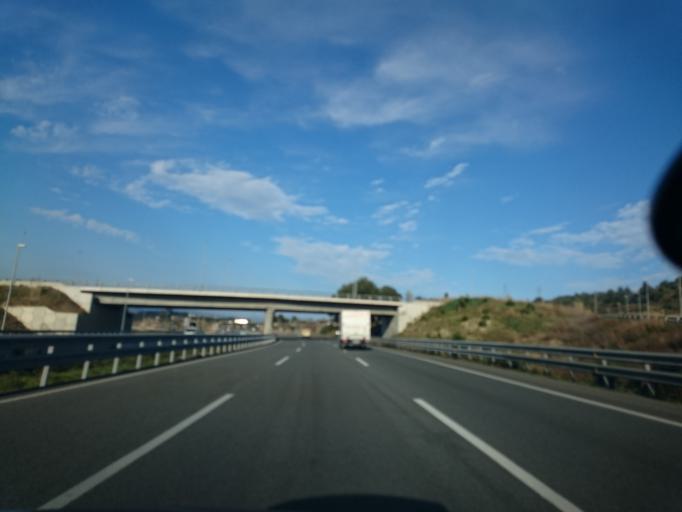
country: ES
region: Catalonia
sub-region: Provincia de Barcelona
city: Sant Sadurni d'Anoia
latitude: 41.4135
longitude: 1.7873
